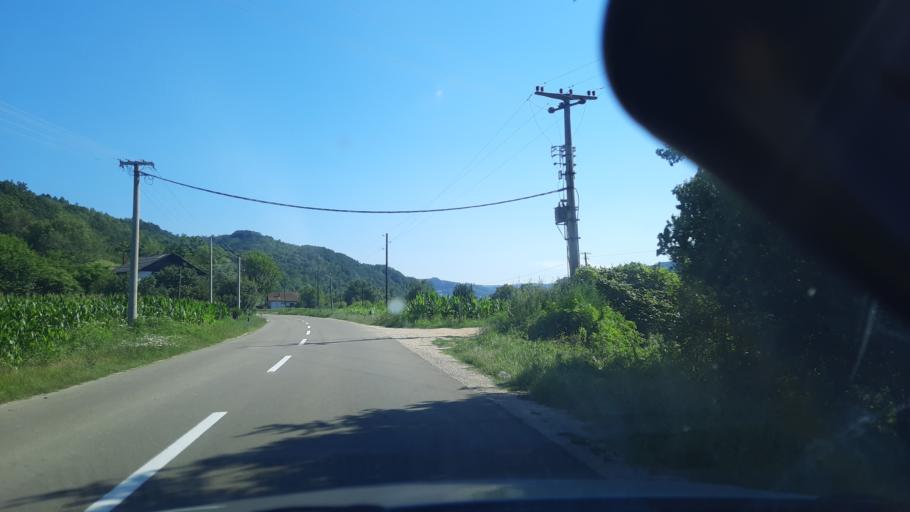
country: RS
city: Turija
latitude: 44.5196
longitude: 21.6396
